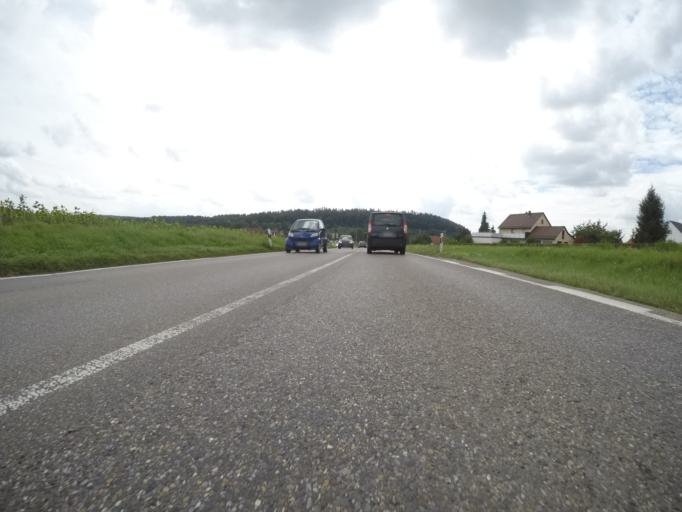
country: DE
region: Baden-Wuerttemberg
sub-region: Regierungsbezirk Stuttgart
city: Nufringen
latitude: 48.6252
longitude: 8.8970
